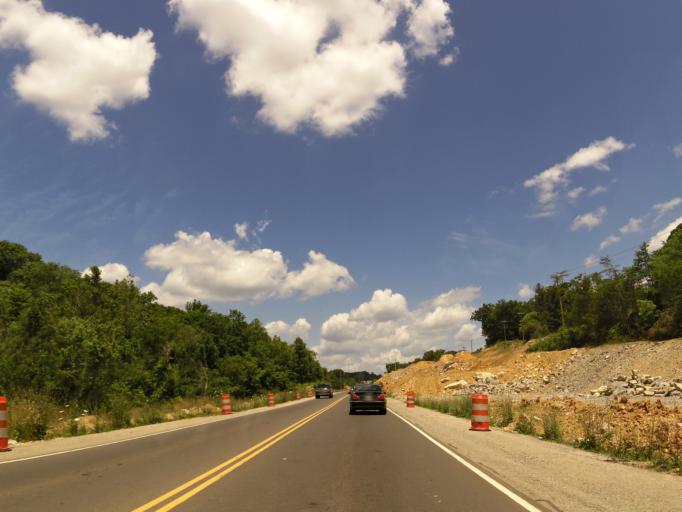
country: US
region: Tennessee
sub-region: Union County
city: Condon
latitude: 36.1106
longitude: -83.9110
